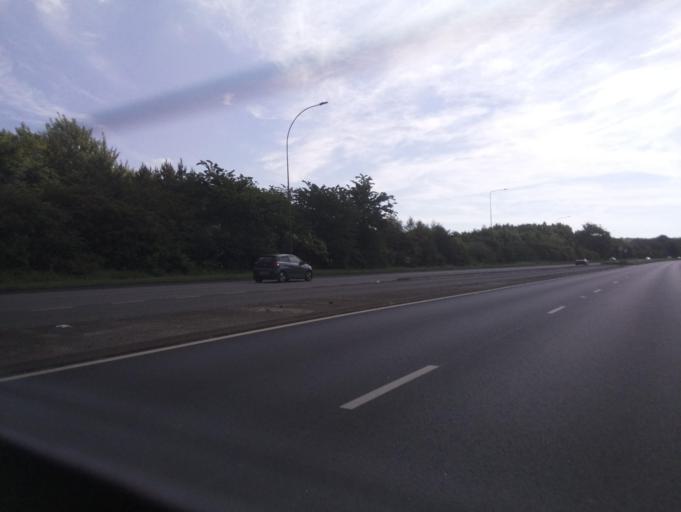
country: GB
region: England
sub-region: North Lincolnshire
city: Manton
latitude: 53.5626
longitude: -0.6020
